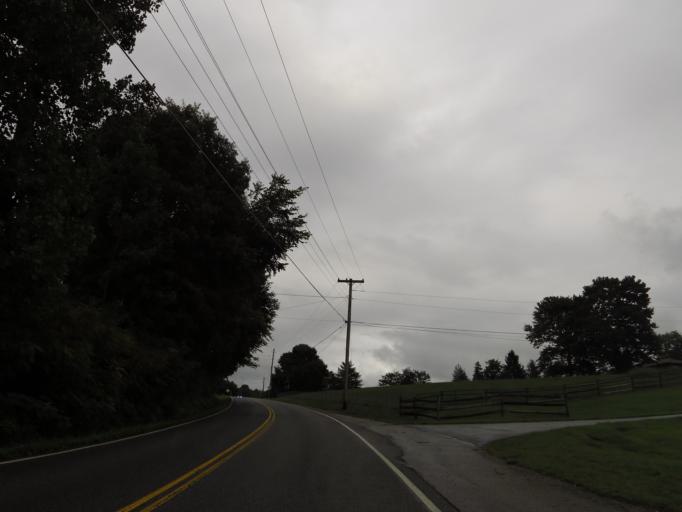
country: US
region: Tennessee
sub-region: Blount County
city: Wildwood
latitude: 35.7855
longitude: -83.8797
